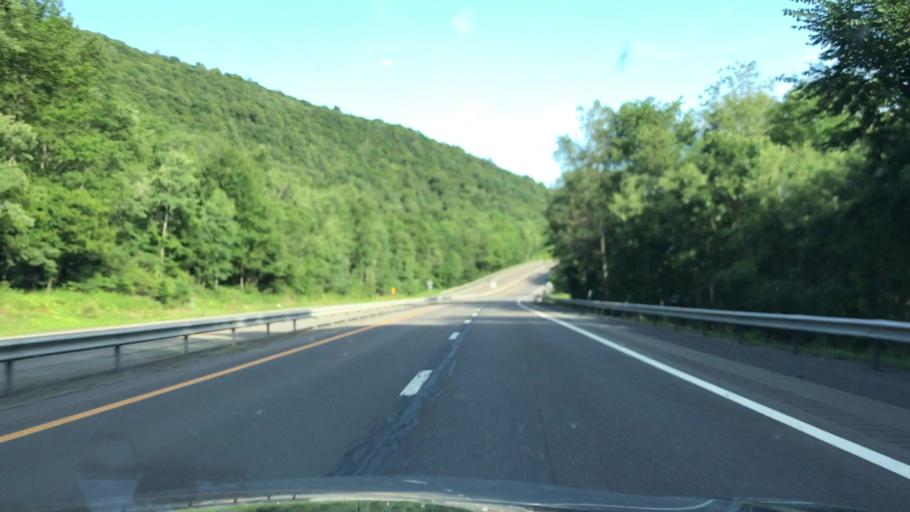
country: US
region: New York
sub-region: Delaware County
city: Hancock
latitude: 41.9648
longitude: -75.3217
